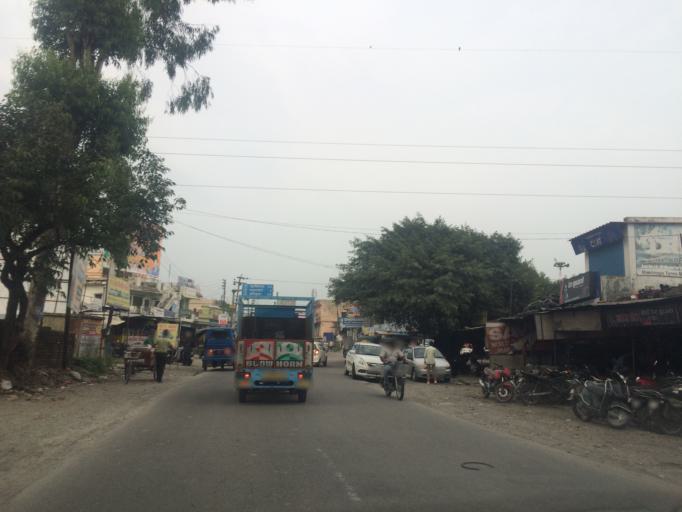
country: IN
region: Uttarakhand
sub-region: Dehradun
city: Doiwala
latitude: 30.1842
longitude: 78.1437
